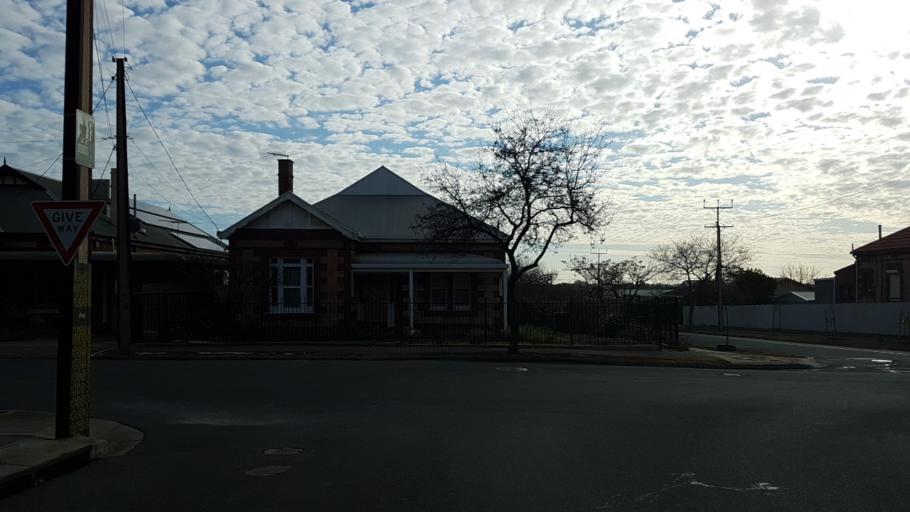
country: AU
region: South Australia
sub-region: Prospect
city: Prospect
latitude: -34.8905
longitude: 138.5898
